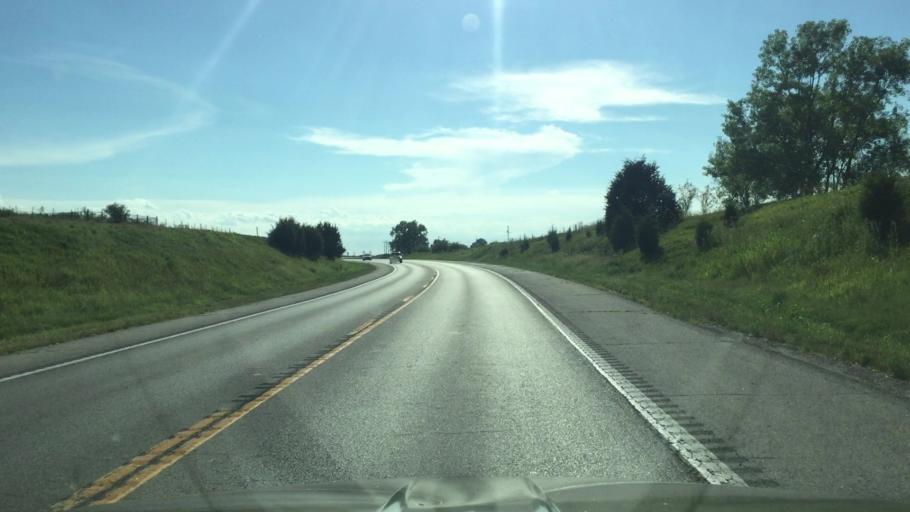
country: US
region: Missouri
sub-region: Pettis County
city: Sedalia
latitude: 38.6952
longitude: -93.1348
